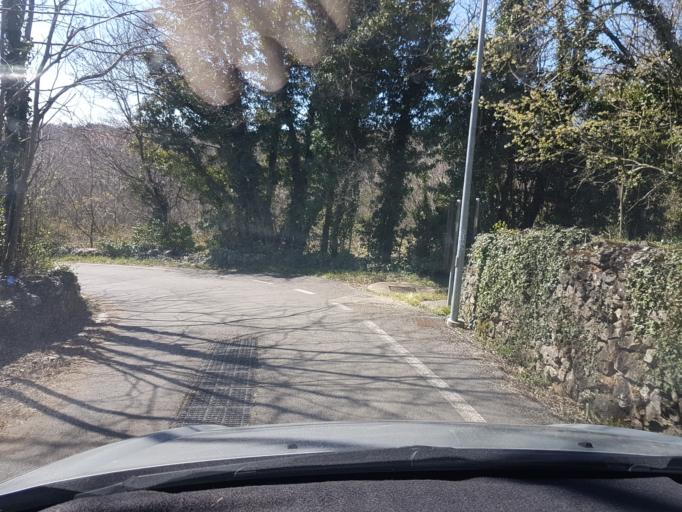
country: IT
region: Friuli Venezia Giulia
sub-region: Provincia di Trieste
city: Santa Croce
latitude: 45.7637
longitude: 13.7063
